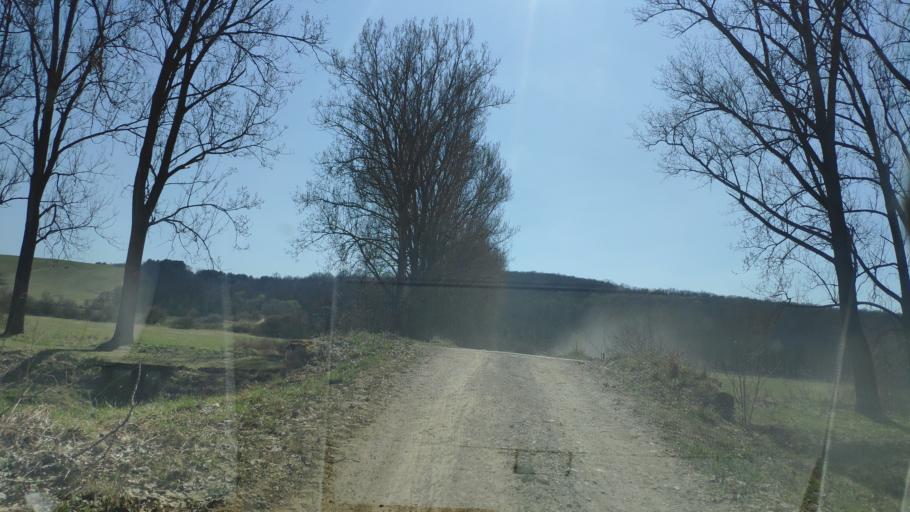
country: SK
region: Kosicky
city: Moldava nad Bodvou
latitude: 48.5690
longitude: 20.9442
